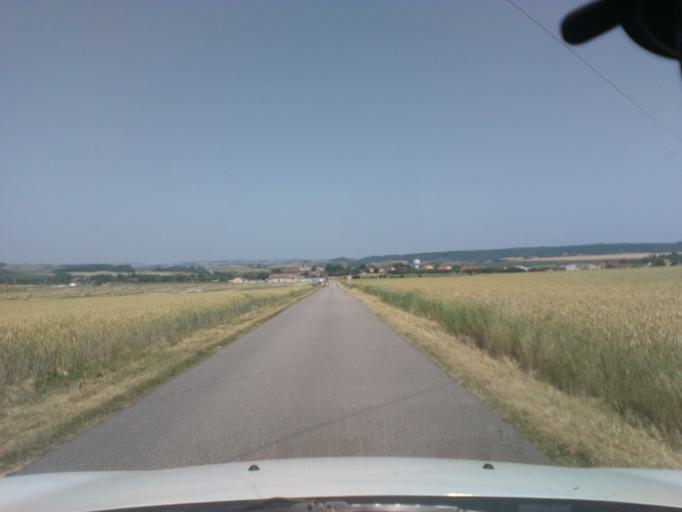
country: FR
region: Lorraine
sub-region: Departement des Vosges
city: Mirecourt
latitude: 48.3149
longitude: 6.1129
